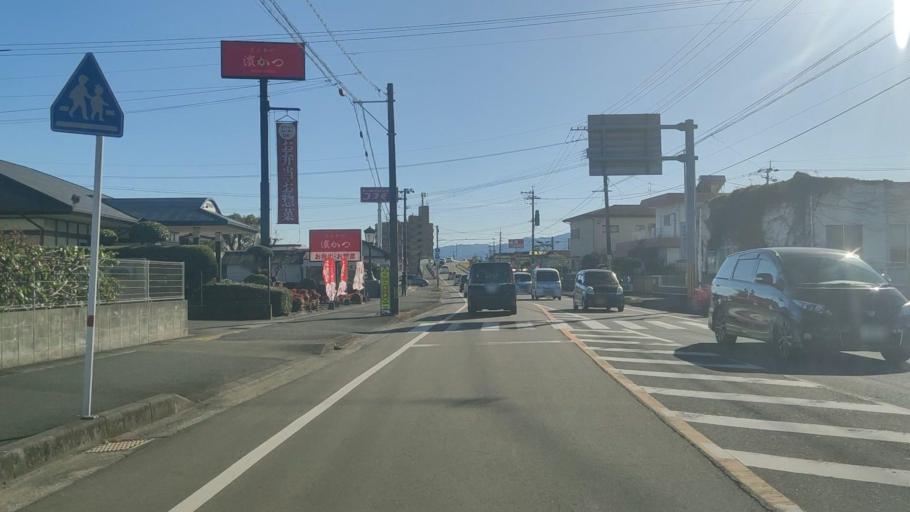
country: JP
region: Miyazaki
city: Miyazaki-shi
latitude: 31.8853
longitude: 131.4287
